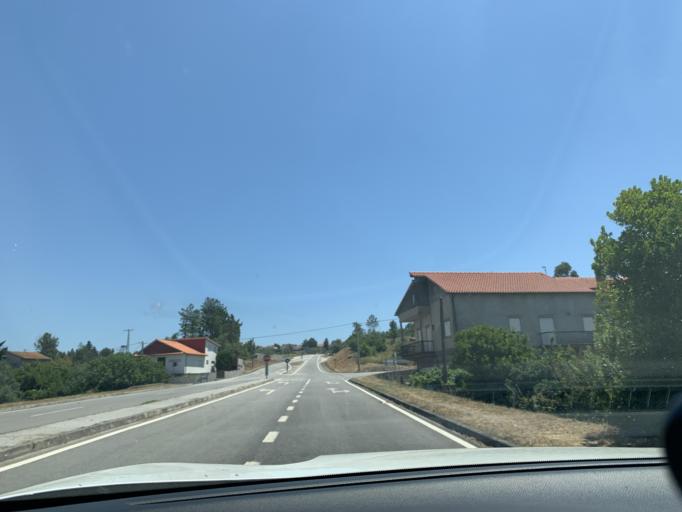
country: PT
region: Viseu
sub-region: Mangualde
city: Mangualde
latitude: 40.5843
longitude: -7.7568
